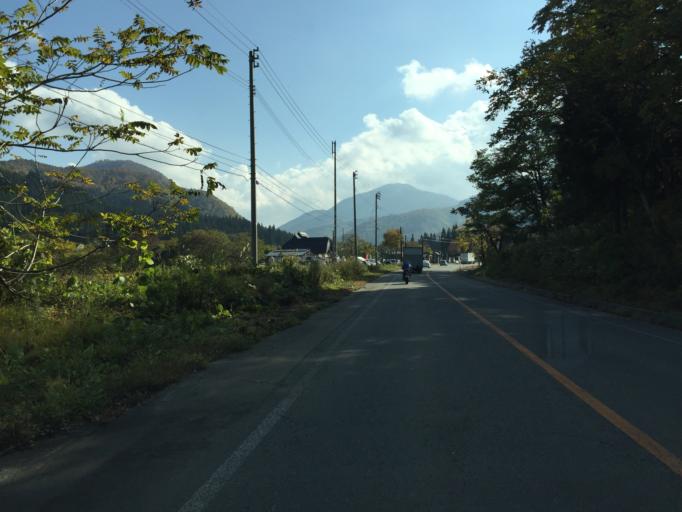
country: JP
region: Yamagata
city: Yonezawa
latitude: 37.8794
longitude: 139.9839
